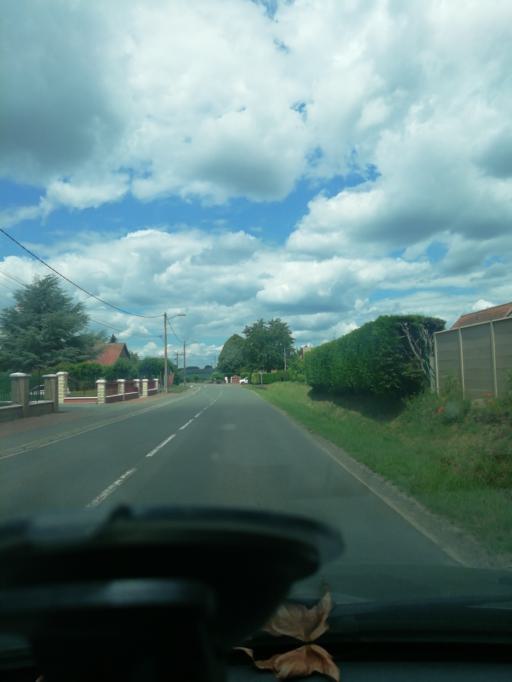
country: FR
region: Nord-Pas-de-Calais
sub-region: Departement du Nord
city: Lewarde
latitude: 50.3134
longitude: 3.1670
